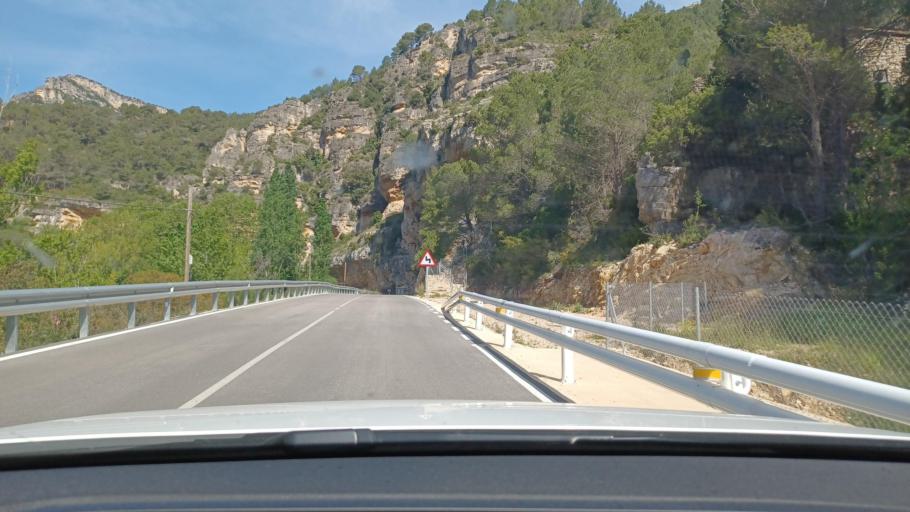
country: ES
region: Valencia
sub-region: Provincia de Castello
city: Rosell
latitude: 40.6714
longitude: 0.2397
